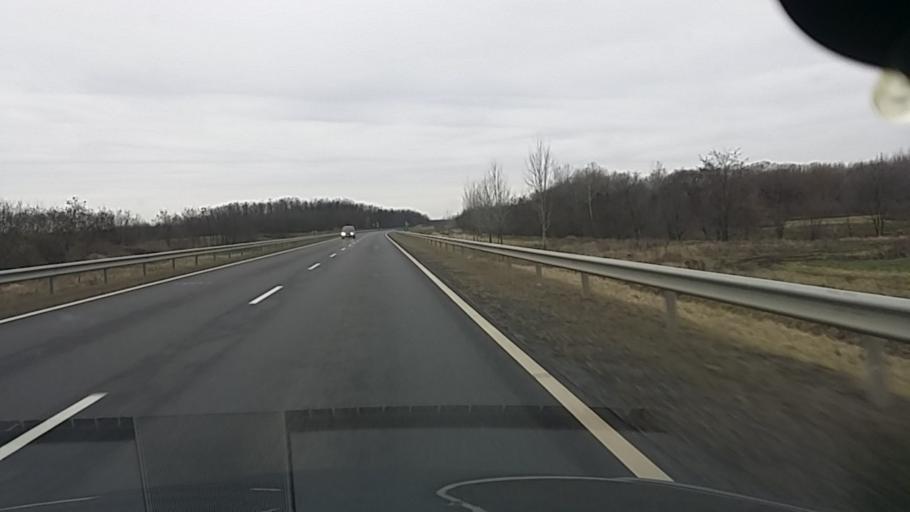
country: HU
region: Szabolcs-Szatmar-Bereg
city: Napkor
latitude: 47.9297
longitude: 21.8194
